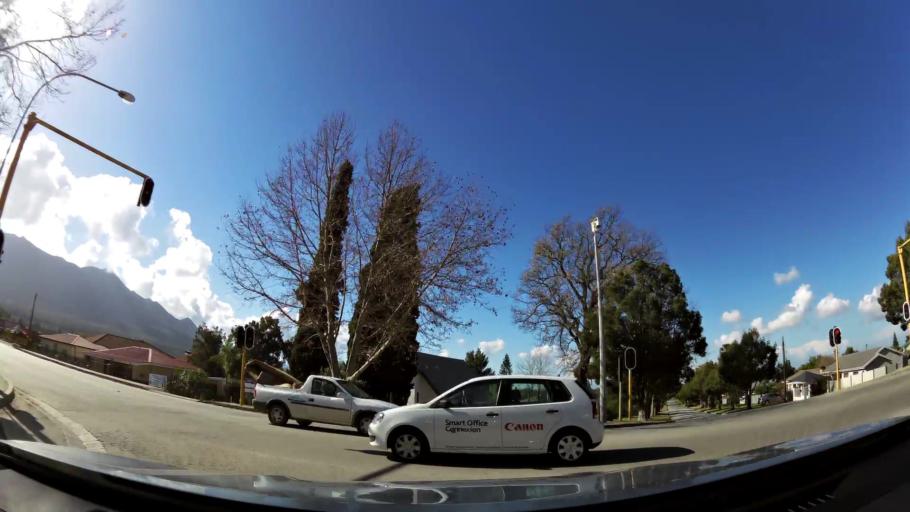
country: ZA
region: Western Cape
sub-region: Eden District Municipality
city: George
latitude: -33.9451
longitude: 22.4115
